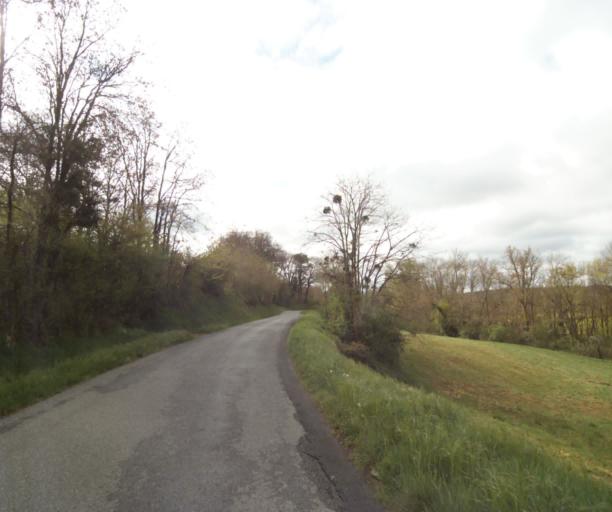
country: FR
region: Midi-Pyrenees
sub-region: Departement de l'Ariege
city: Saverdun
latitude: 43.2398
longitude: 1.5619
